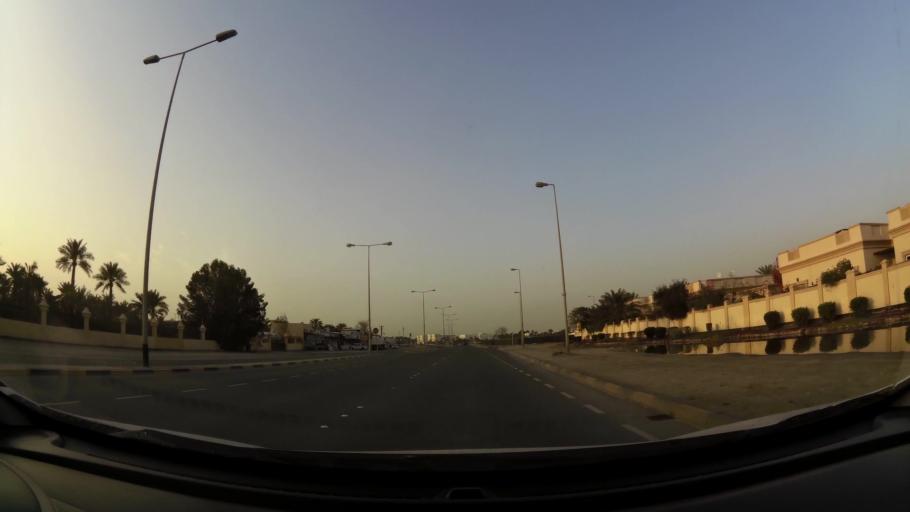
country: BH
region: Central Governorate
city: Madinat Hamad
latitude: 26.1857
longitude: 50.4660
